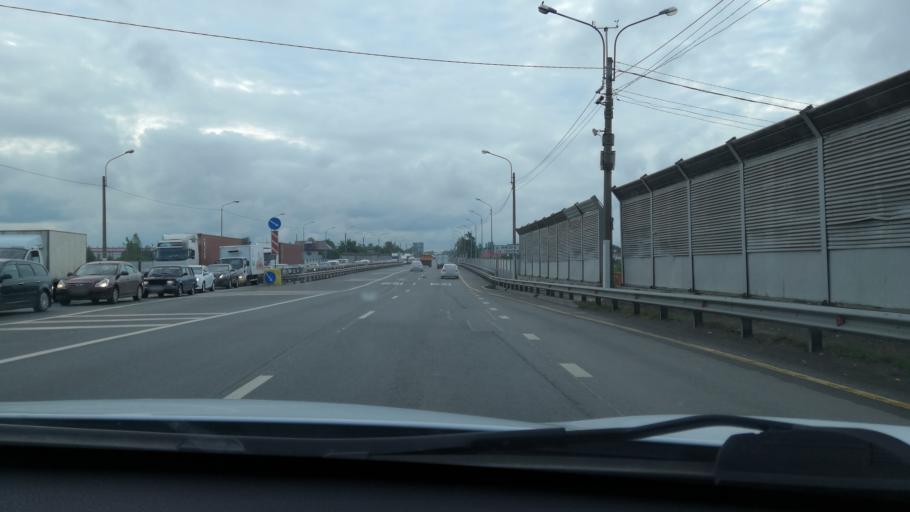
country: RU
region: St.-Petersburg
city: Kolpino
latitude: 59.7037
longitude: 30.5784
